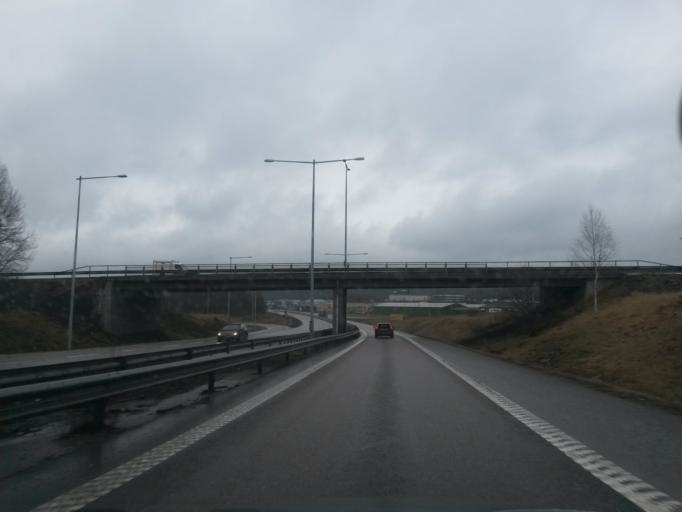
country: SE
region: Vaestra Goetaland
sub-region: Uddevalla Kommun
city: Uddevalla
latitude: 58.3485
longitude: 11.9846
